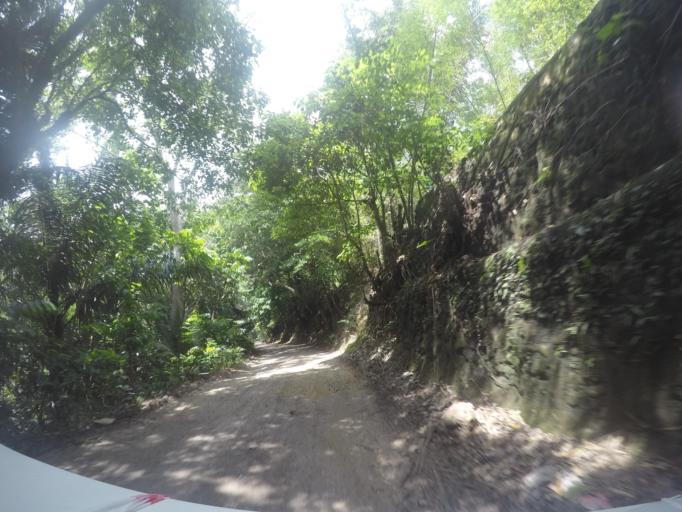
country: TL
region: Baucau
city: Venilale
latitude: -8.5735
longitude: 126.3887
